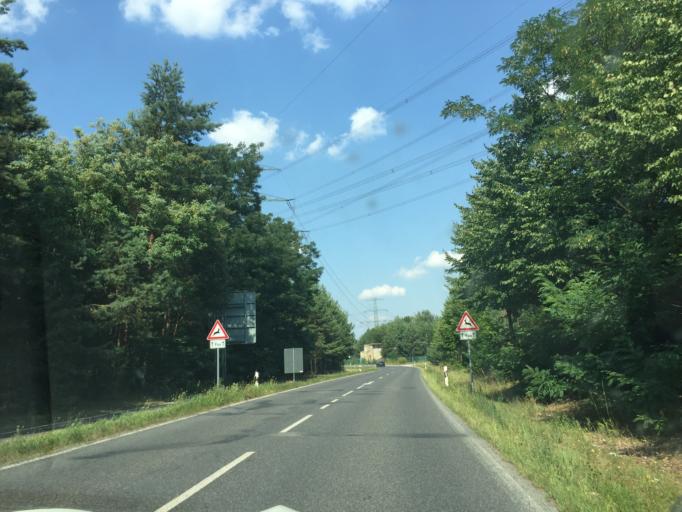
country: DE
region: Saxony
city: Boxberg
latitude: 51.4102
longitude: 14.5548
